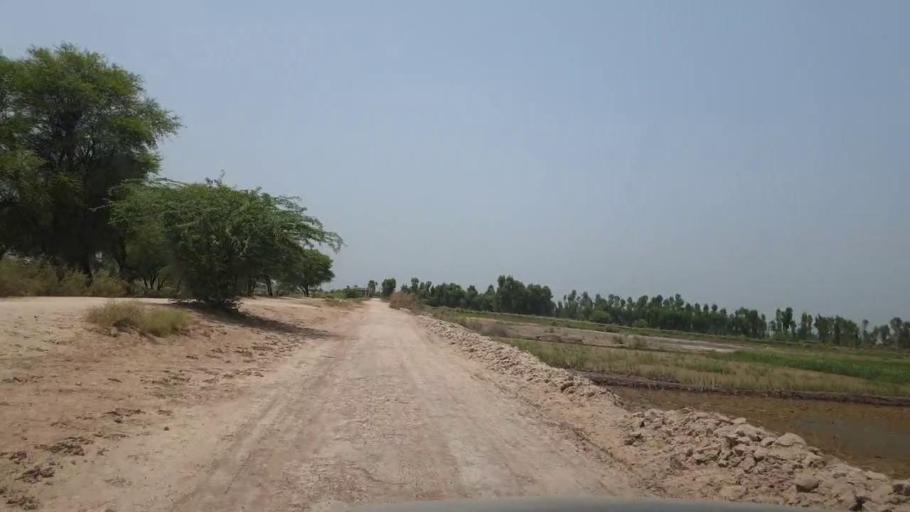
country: PK
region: Sindh
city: Garhi Yasin
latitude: 27.8863
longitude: 68.4333
